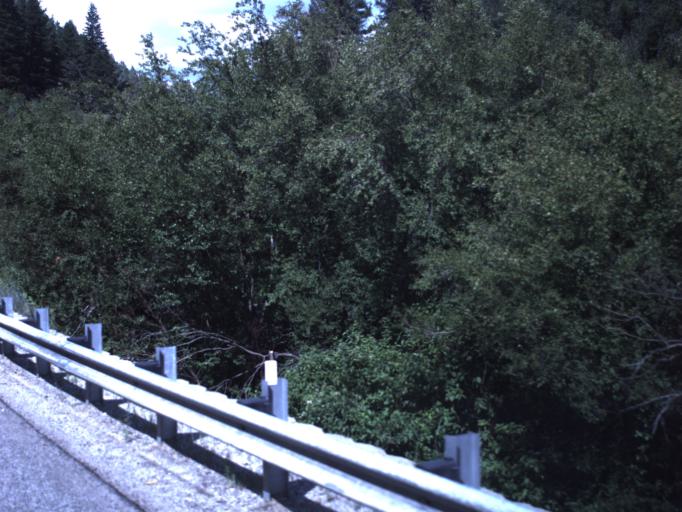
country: US
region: Utah
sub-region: Cache County
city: North Logan
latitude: 41.8055
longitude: -111.6307
